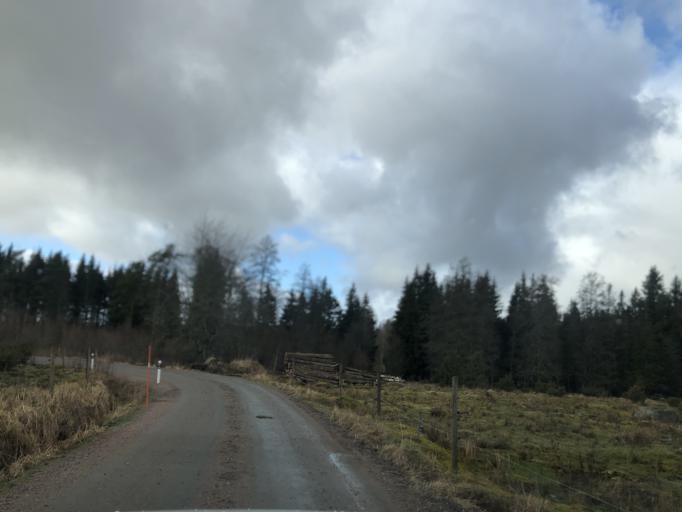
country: SE
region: Vaestra Goetaland
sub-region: Ulricehamns Kommun
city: Ulricehamn
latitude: 57.8288
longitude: 13.2455
